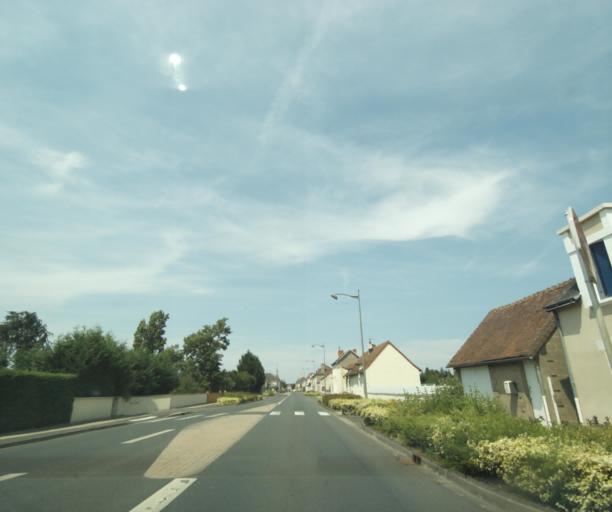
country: FR
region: Poitou-Charentes
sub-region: Departement de la Vienne
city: Dange-Saint-Romain
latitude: 46.9332
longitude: 0.6052
